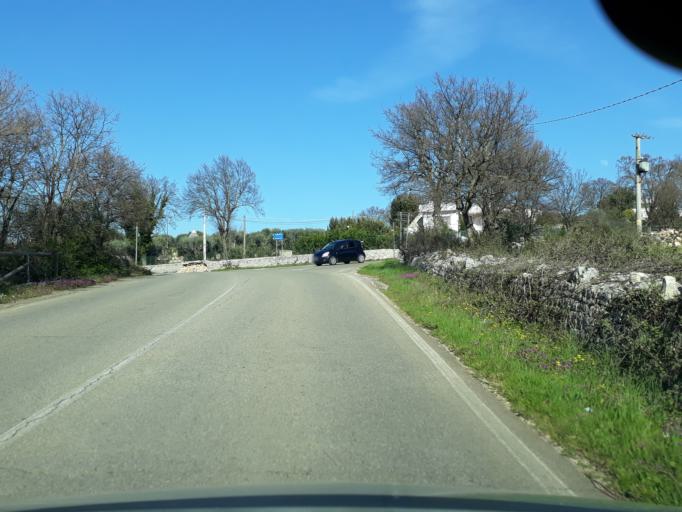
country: IT
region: Apulia
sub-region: Provincia di Bari
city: Cozzana
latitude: 40.8578
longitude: 17.2567
